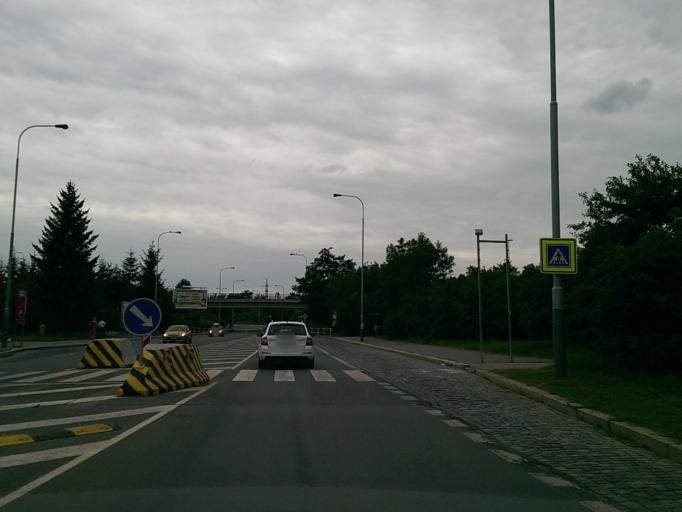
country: CZ
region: Praha
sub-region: Praha 14
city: Dolni Pocernice
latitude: 50.0475
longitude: 14.5657
